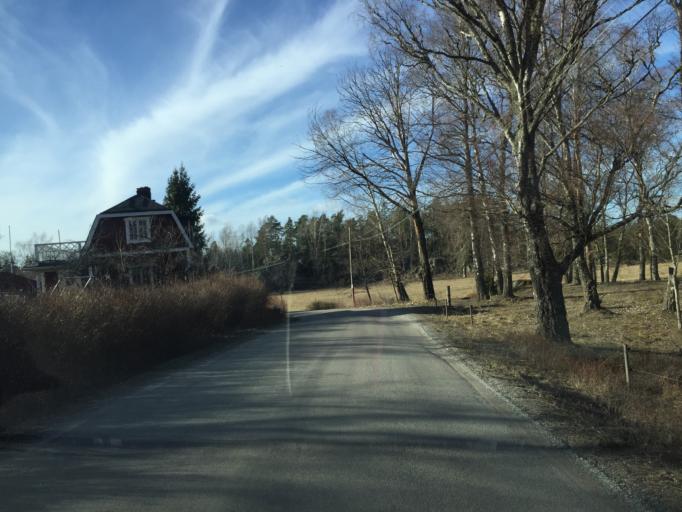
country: SE
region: Stockholm
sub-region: Nynashamns Kommun
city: Osmo
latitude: 59.0450
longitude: 17.8259
